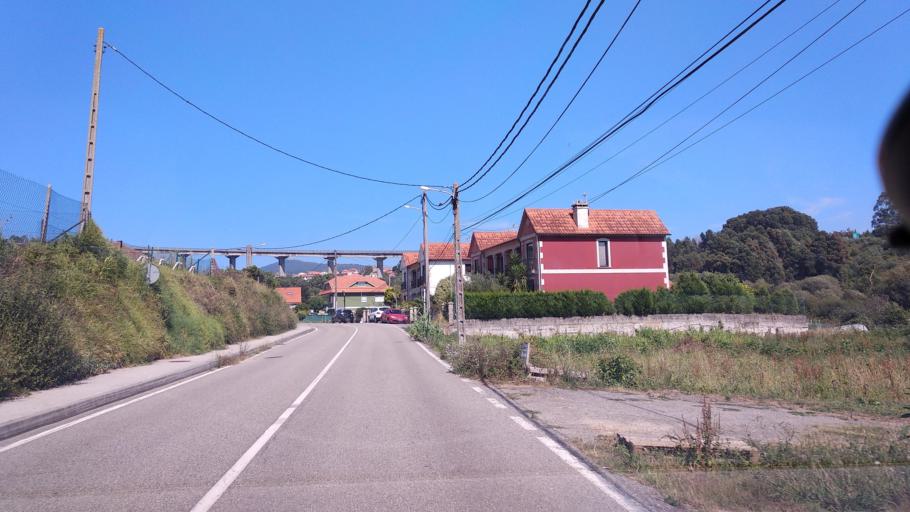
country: ES
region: Galicia
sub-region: Provincia de Pontevedra
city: Moana
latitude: 42.2784
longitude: -8.7567
